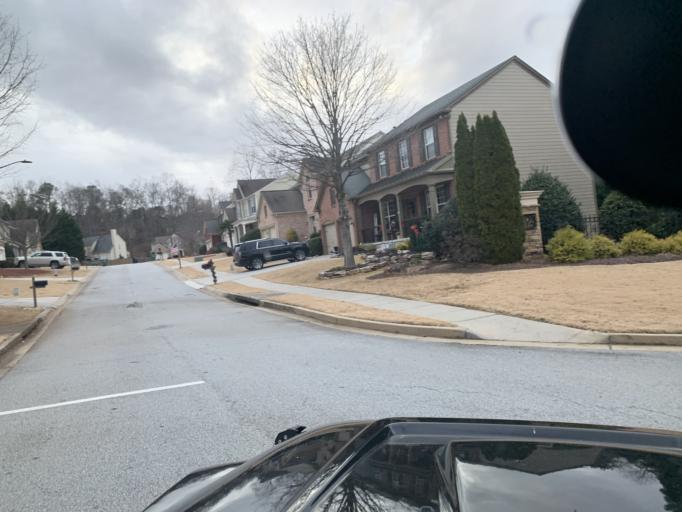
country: US
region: Georgia
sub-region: Cherokee County
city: Woodstock
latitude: 34.0992
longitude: -84.4599
